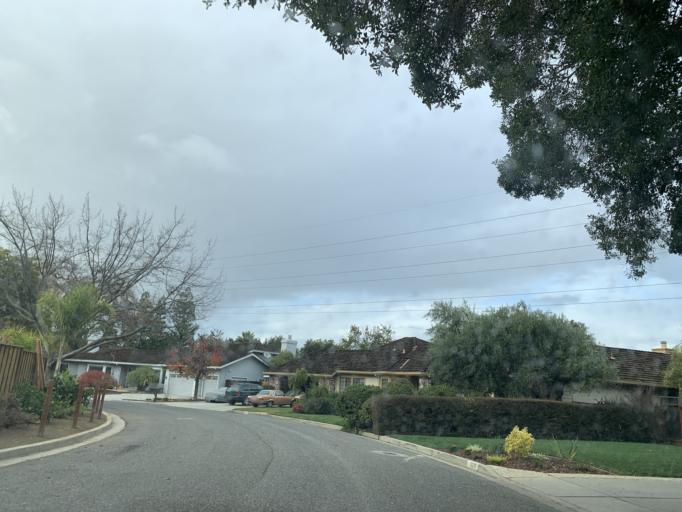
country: US
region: California
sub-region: Santa Clara County
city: Saratoga
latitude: 37.2686
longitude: -121.9914
